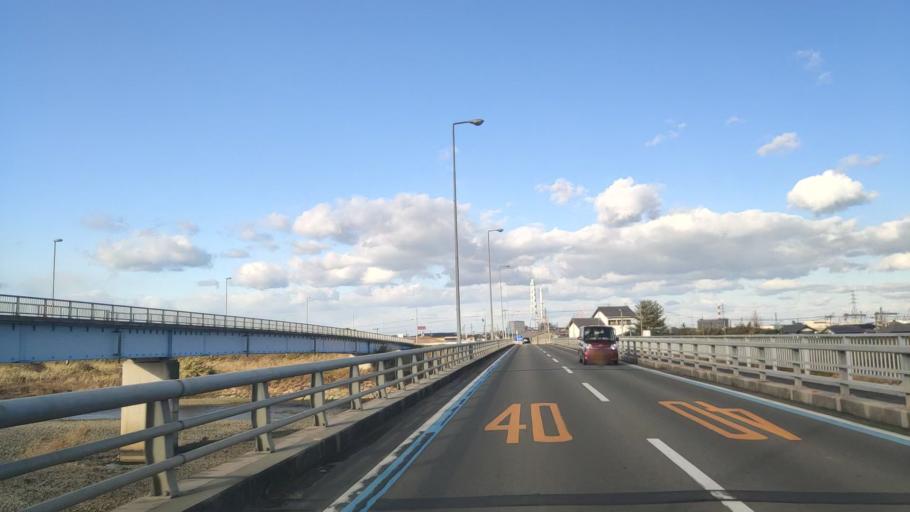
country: JP
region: Ehime
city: Saijo
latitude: 33.9124
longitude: 133.1615
